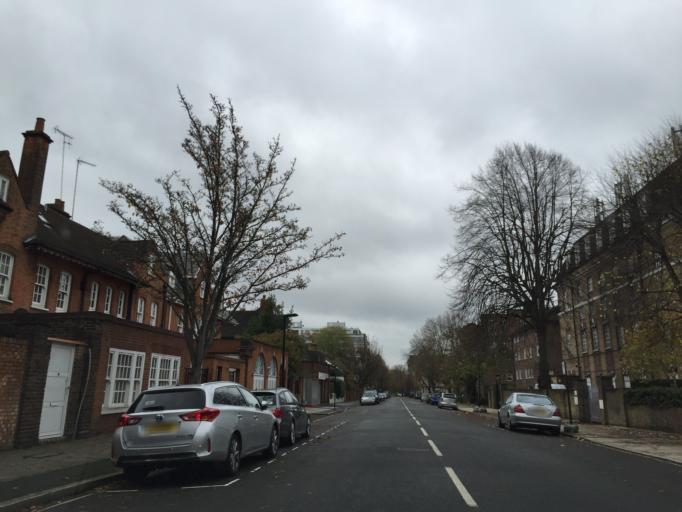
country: GB
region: England
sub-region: Greater London
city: Belsize Park
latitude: 51.5370
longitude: -0.1682
